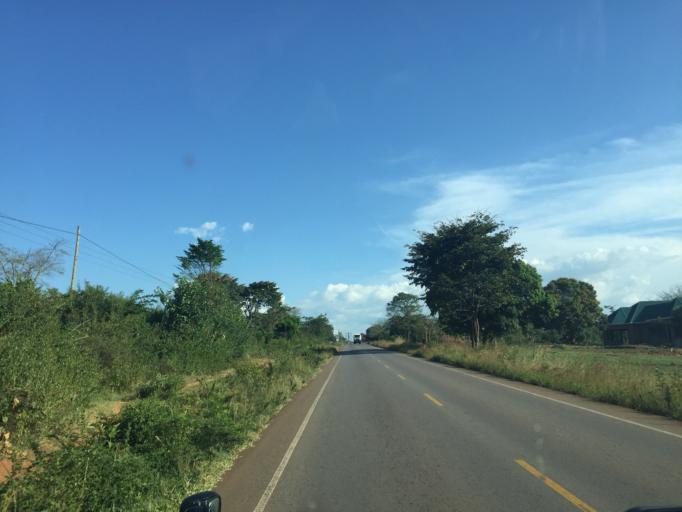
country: UG
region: Central Region
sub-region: Nakasongola District
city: Nakasongola
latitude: 1.2546
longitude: 32.4559
